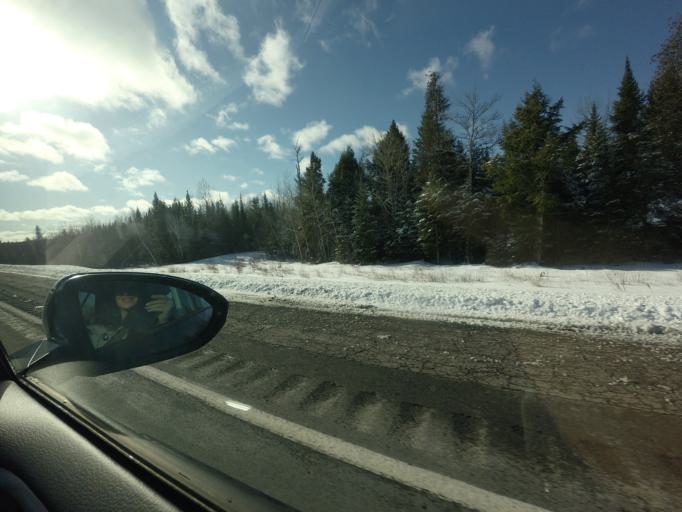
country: CA
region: New Brunswick
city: Fredericton
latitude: 45.8838
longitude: -66.6393
